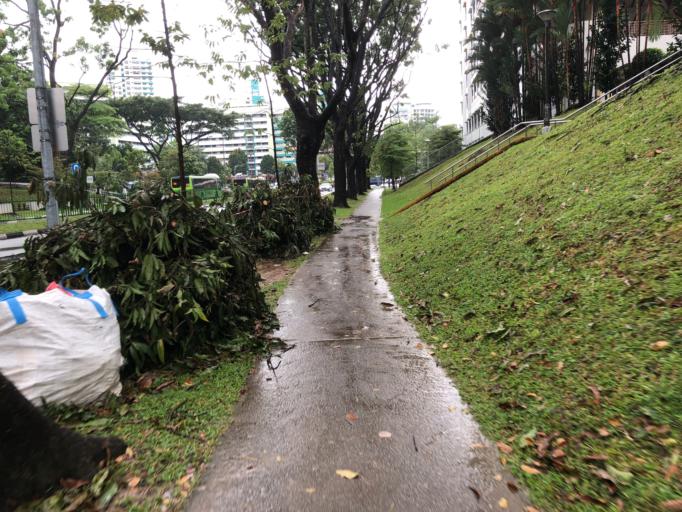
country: SG
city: Singapore
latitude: 1.3482
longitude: 103.7553
